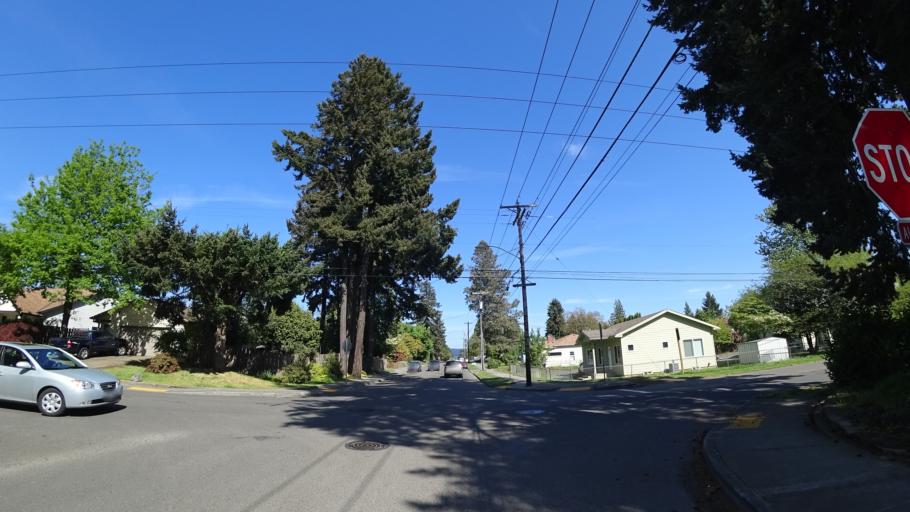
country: US
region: Oregon
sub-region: Clackamas County
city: Milwaukie
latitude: 45.4480
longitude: -122.6223
